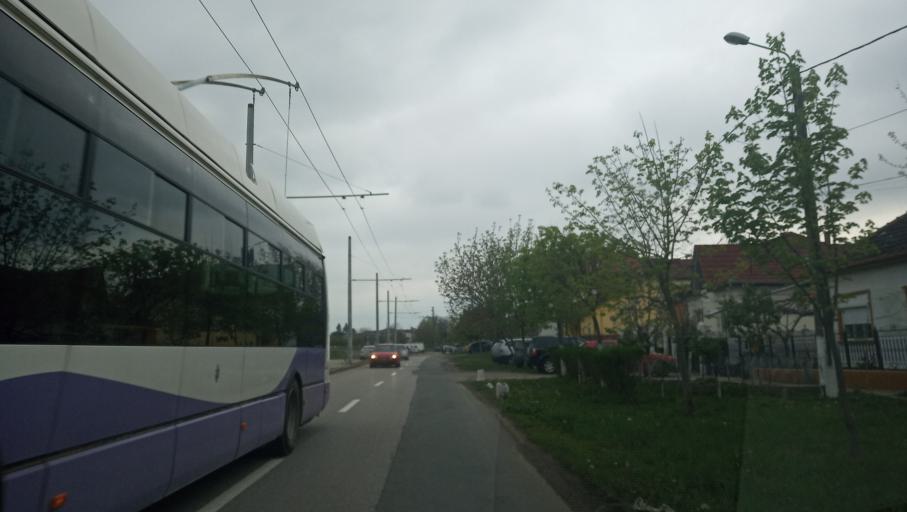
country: RO
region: Timis
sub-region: Comuna Ghiroda
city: Ghiroda
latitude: 45.7663
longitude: 21.2687
